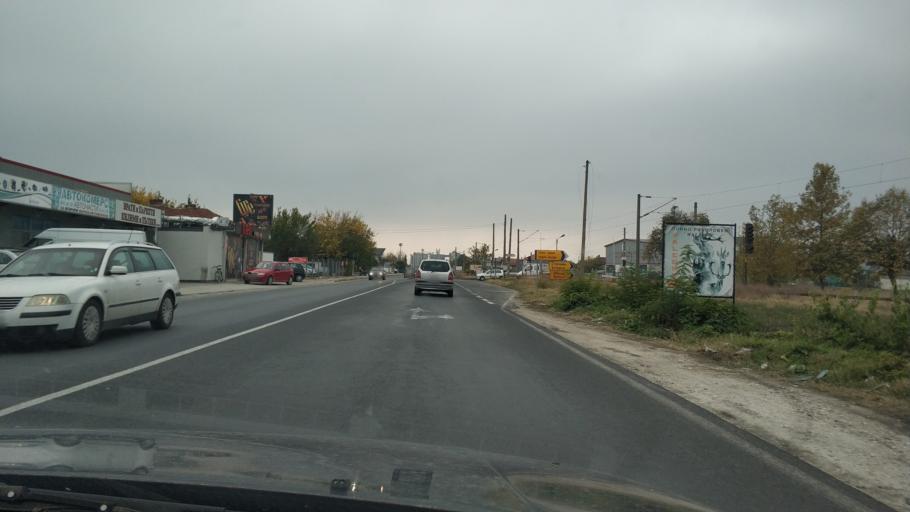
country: BG
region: Plovdiv
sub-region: Obshtina Plovdiv
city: Plovdiv
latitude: 42.2375
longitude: 24.7235
